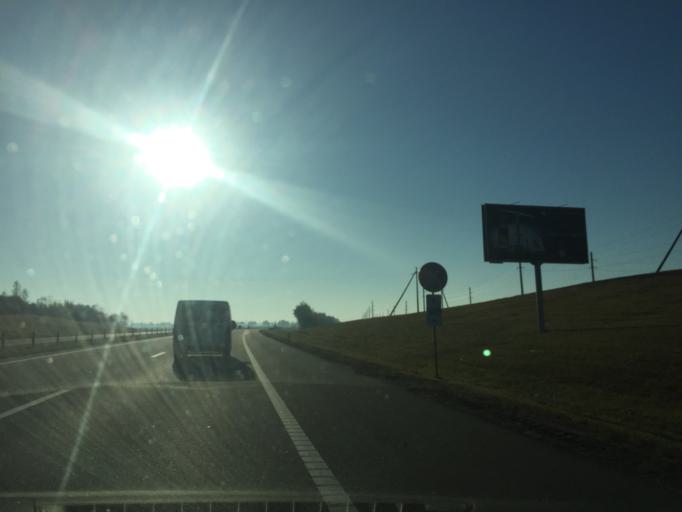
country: BY
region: Minsk
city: Luhavaya Slabada
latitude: 53.7748
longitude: 27.8550
